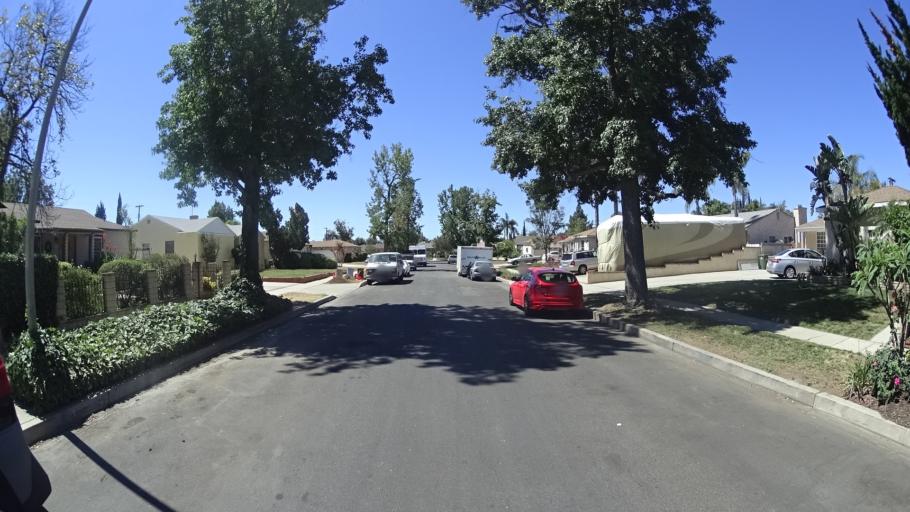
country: US
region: California
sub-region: Los Angeles County
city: San Fernando
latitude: 34.2555
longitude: -118.4599
